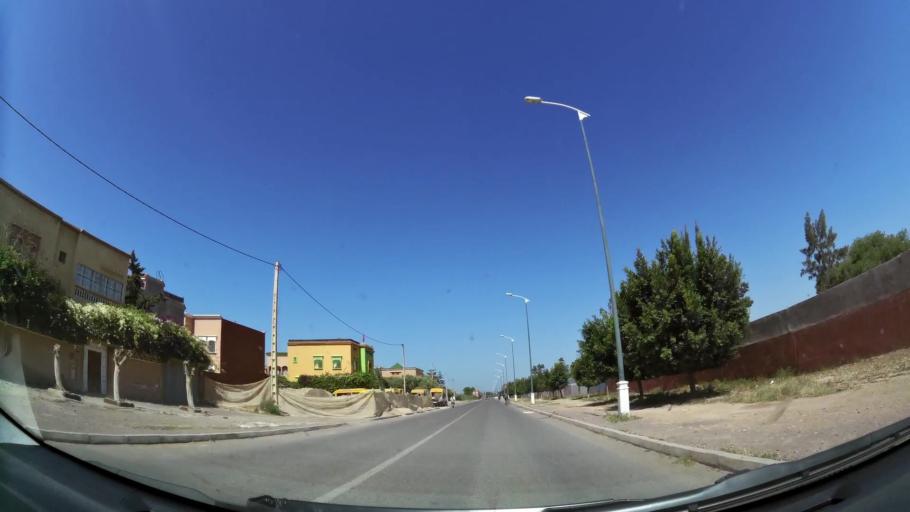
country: MA
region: Souss-Massa-Draa
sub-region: Inezgane-Ait Mellou
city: Inezgane
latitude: 30.3262
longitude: -9.5052
